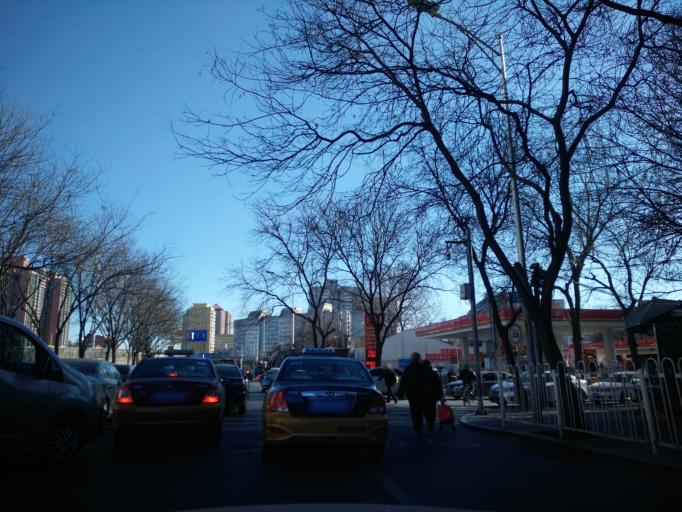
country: CN
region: Beijing
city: Dahongmen
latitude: 39.8556
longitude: 116.4130
